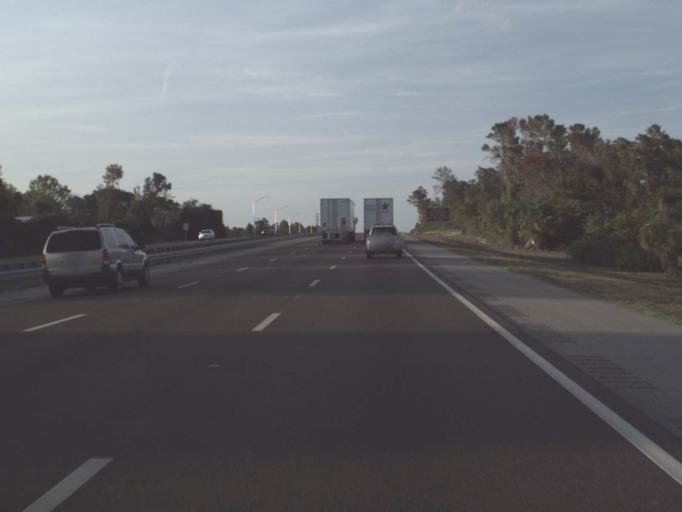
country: US
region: Florida
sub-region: Brevard County
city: Titusville
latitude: 28.6050
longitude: -80.8511
